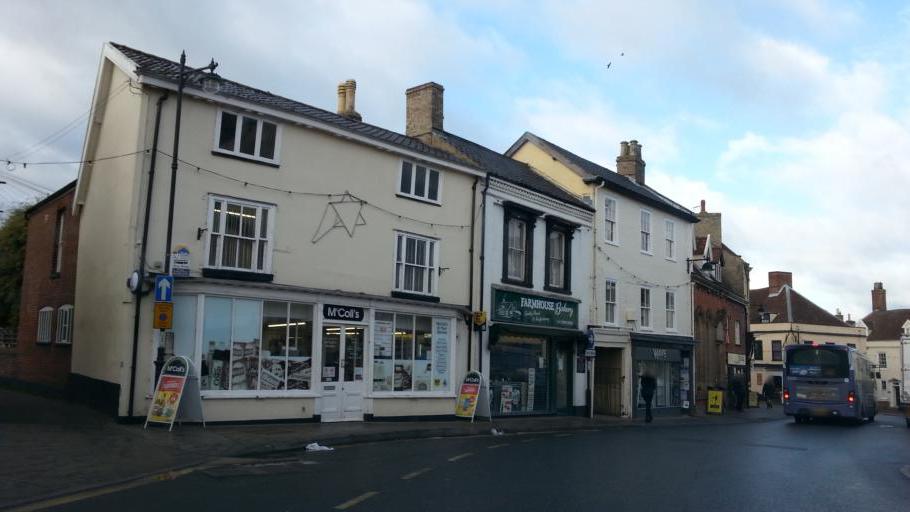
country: GB
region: England
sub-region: Suffolk
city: Bungay
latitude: 52.4556
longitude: 1.4372
